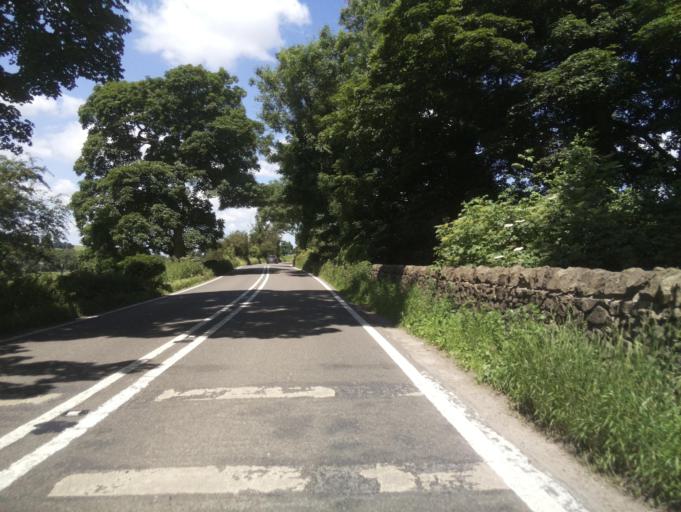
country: GB
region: England
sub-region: Derbyshire
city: Ashbourne
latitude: 53.0665
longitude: -1.7478
